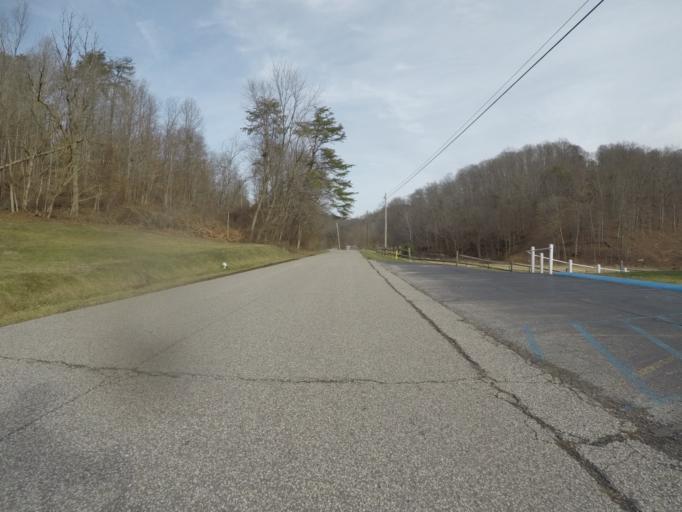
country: US
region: West Virginia
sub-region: Wayne County
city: Lavalette
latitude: 38.3547
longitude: -82.3738
